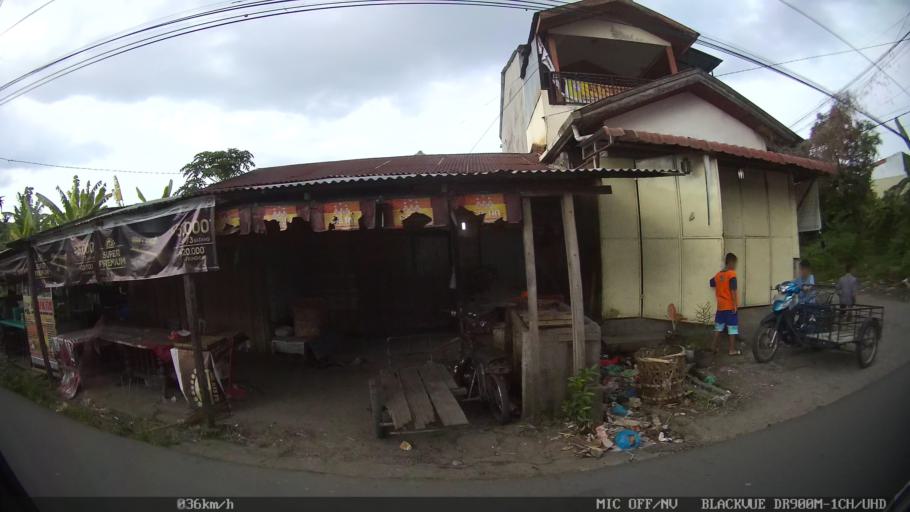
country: ID
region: North Sumatra
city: Sunggal
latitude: 3.5231
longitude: 98.6158
